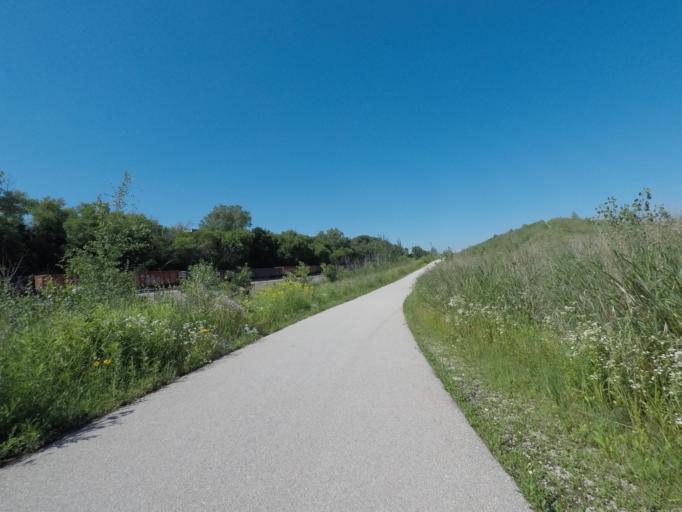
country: US
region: Wisconsin
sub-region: Milwaukee County
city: West Milwaukee
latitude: 43.0266
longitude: -87.9503
